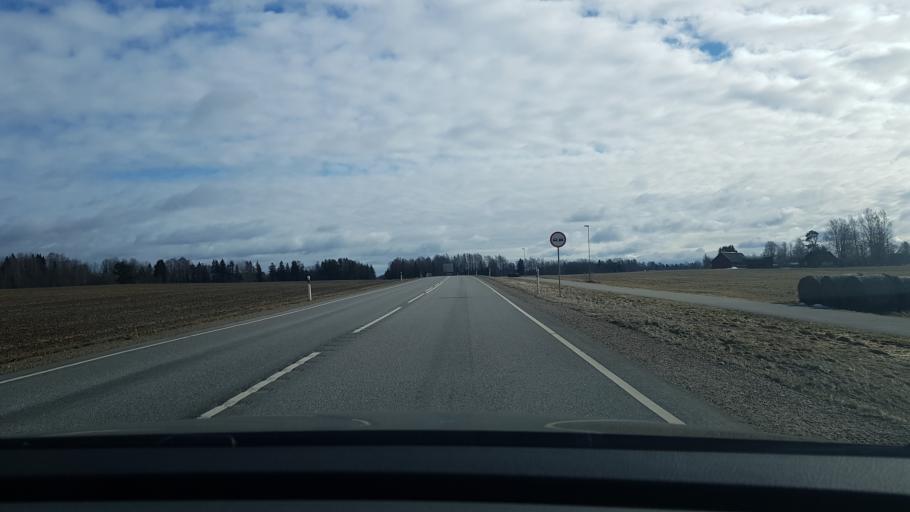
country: EE
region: Paernumaa
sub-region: Saarde vald
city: Kilingi-Nomme
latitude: 58.1553
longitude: 24.9980
